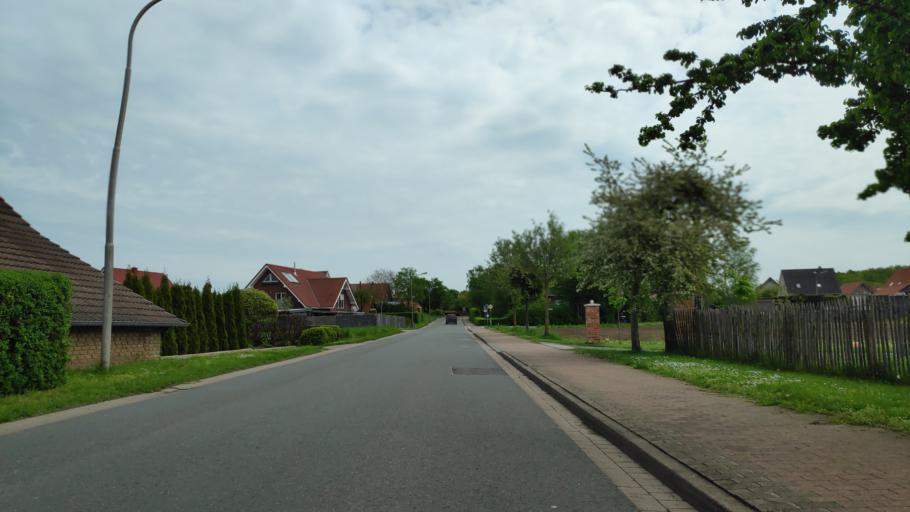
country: DE
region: North Rhine-Westphalia
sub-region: Regierungsbezirk Detmold
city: Petershagen
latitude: 52.3105
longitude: 8.9937
